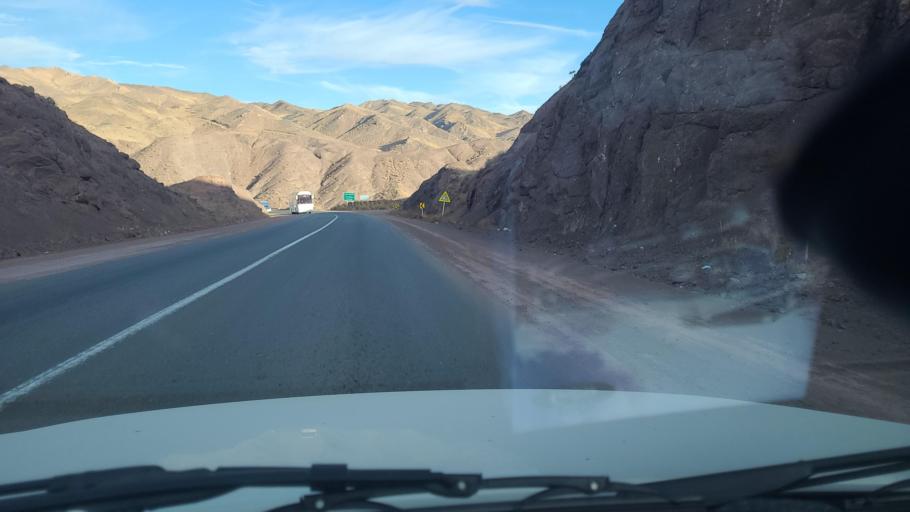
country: IR
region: Razavi Khorasan
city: Sabzevar
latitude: 36.4184
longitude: 57.5625
